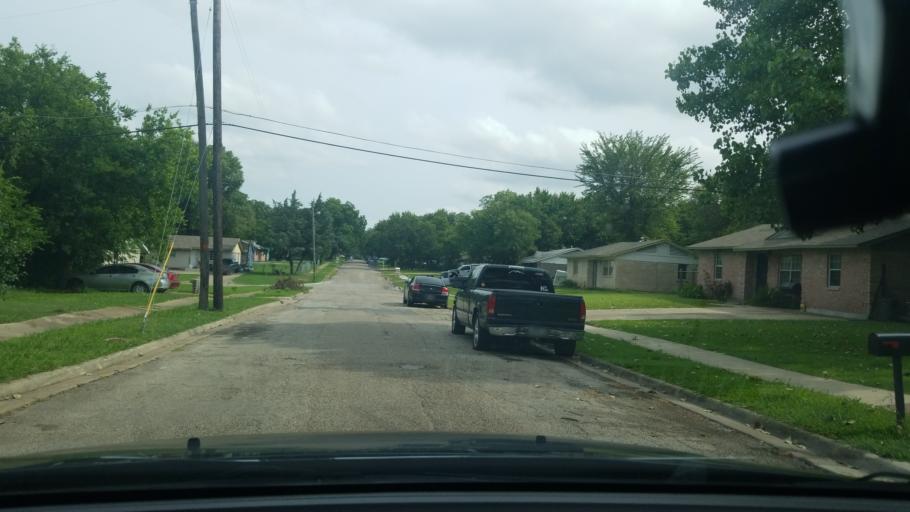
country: US
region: Texas
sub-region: Dallas County
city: Mesquite
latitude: 32.7588
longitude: -96.6259
